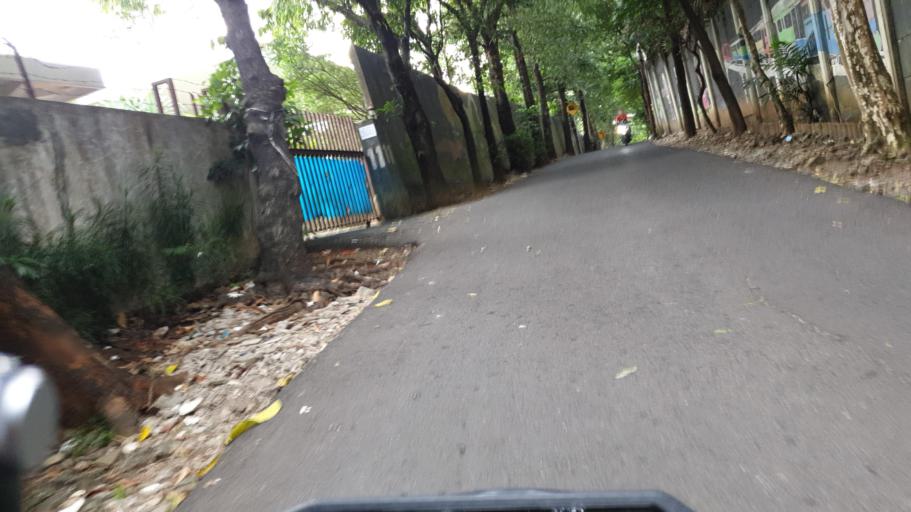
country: ID
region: Banten
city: South Tangerang
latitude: -6.2744
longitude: 106.7926
